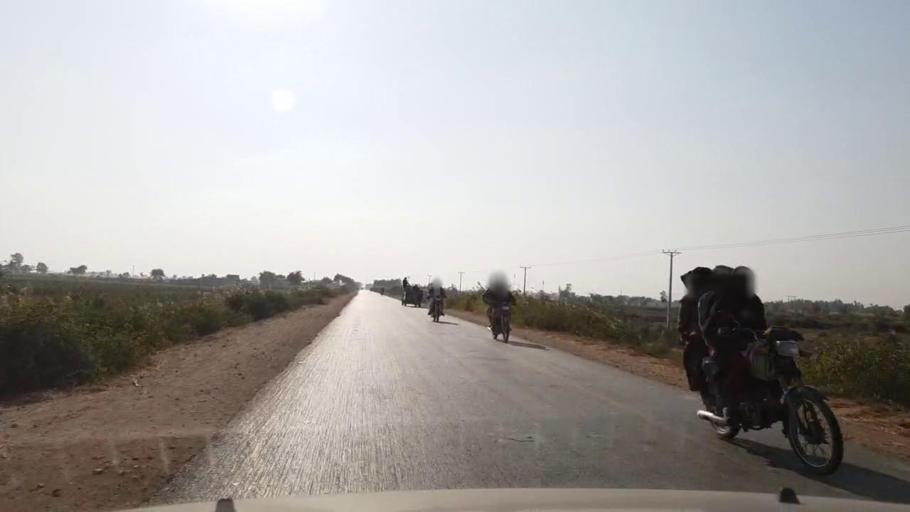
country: PK
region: Sindh
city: Tando Muhammad Khan
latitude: 25.0669
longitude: 68.4710
